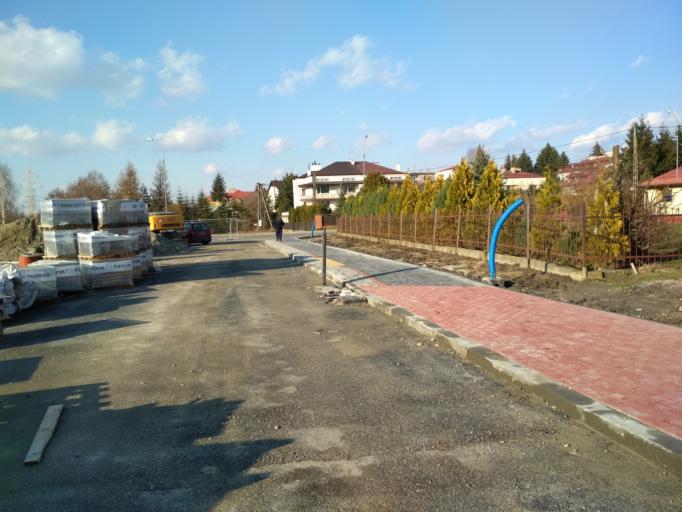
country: PL
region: Subcarpathian Voivodeship
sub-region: Rzeszow
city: Rzeszow
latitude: 50.0488
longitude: 21.9646
